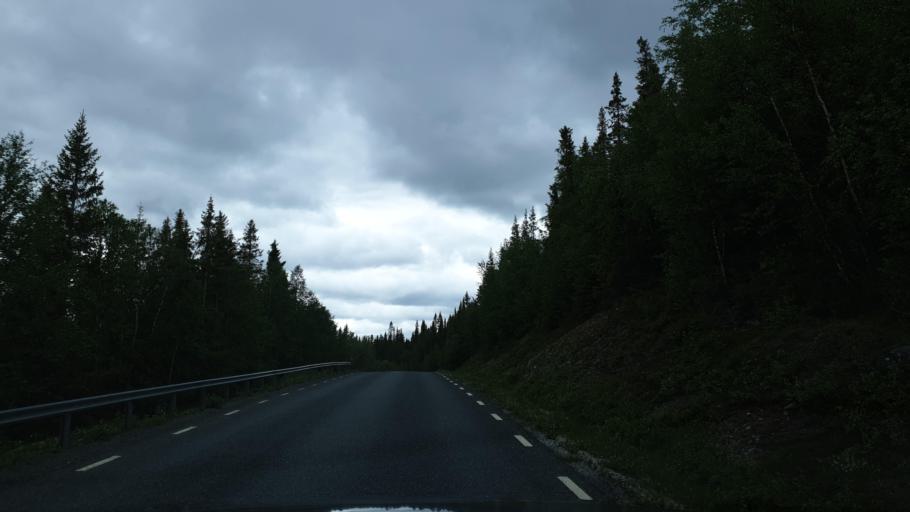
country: SE
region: Vaesterbotten
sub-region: Vilhelmina Kommun
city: Sjoberg
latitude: 65.2603
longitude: 15.3859
